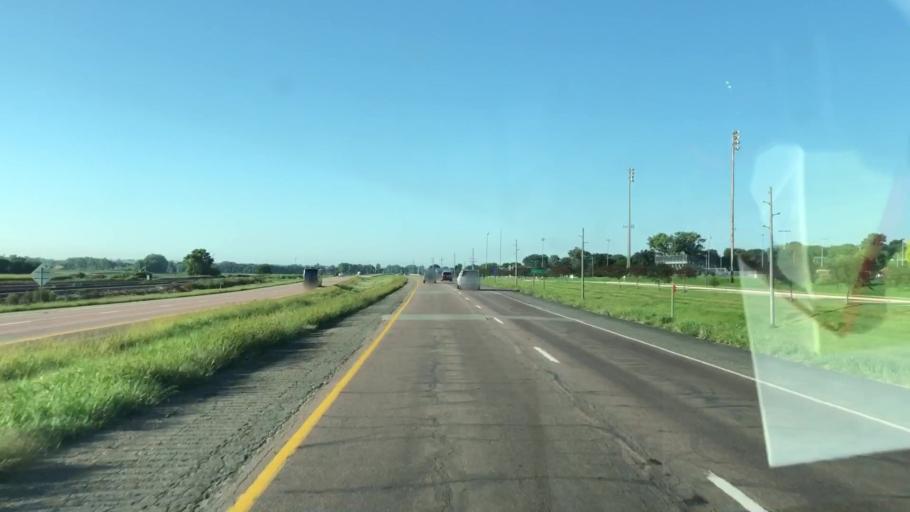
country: US
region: Iowa
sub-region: Woodbury County
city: Sioux City
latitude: 42.6223
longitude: -96.2933
